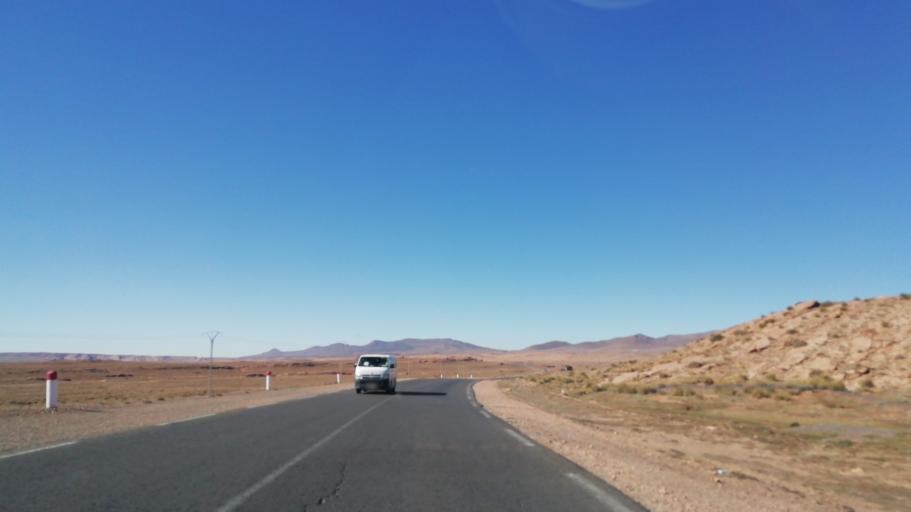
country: DZ
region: El Bayadh
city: El Bayadh
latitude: 33.6109
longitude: 1.2290
